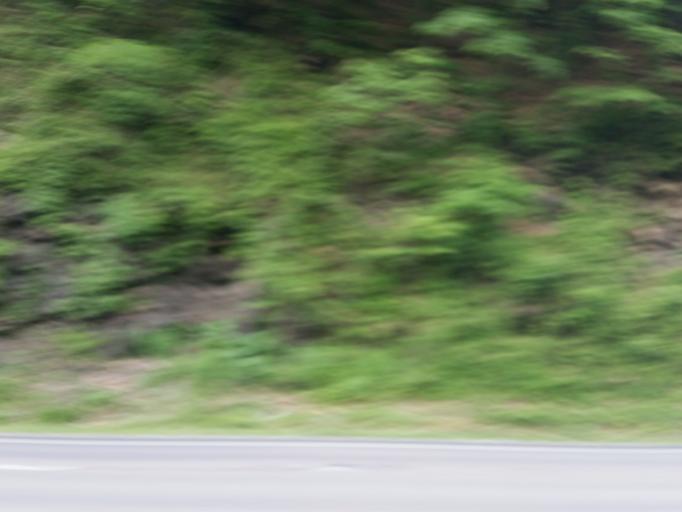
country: US
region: Virginia
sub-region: Washington County
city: Abingdon
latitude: 36.7521
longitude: -82.0566
